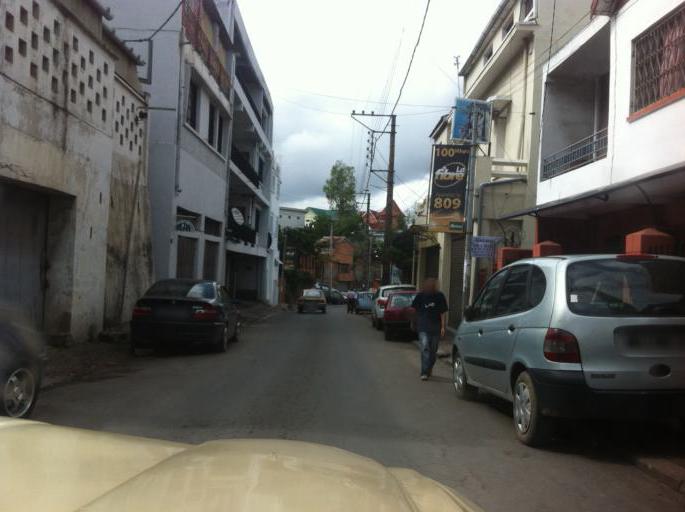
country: MG
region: Analamanga
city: Antananarivo
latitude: -18.9113
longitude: 47.5203
